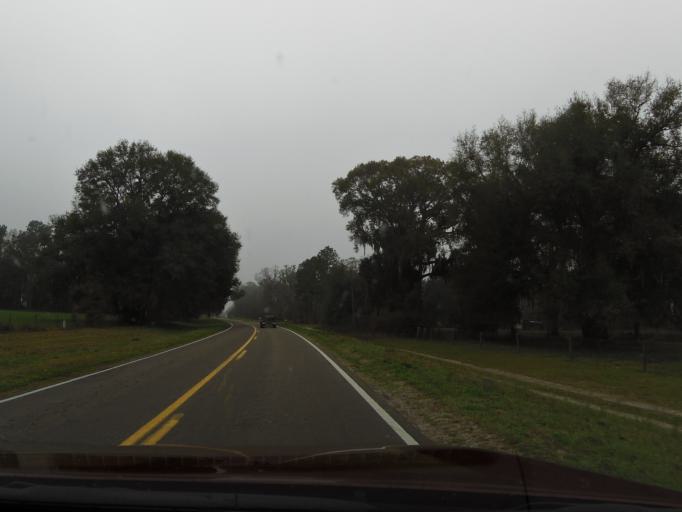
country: US
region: Florida
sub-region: Alachua County
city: Alachua
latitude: 29.8919
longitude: -82.4505
